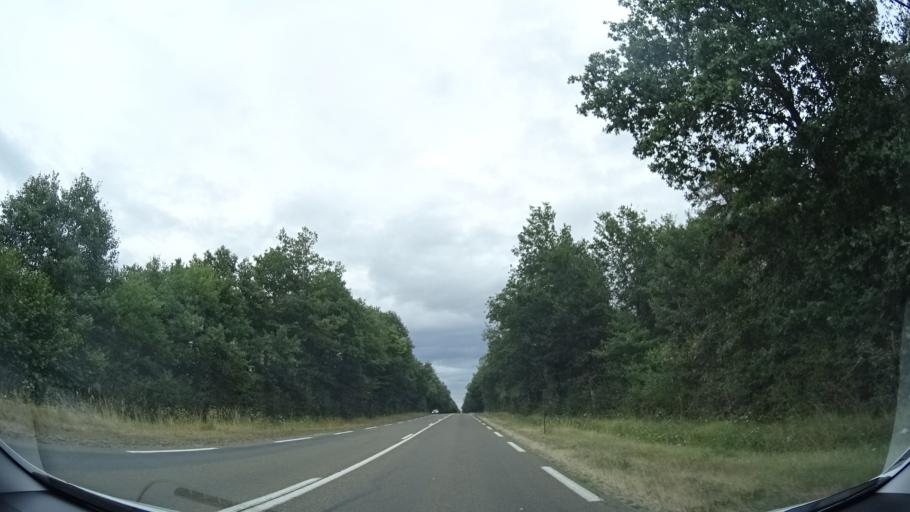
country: FR
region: Centre
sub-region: Departement du Loiret
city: Huisseau-sur-Mauves
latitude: 47.9276
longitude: 1.7317
